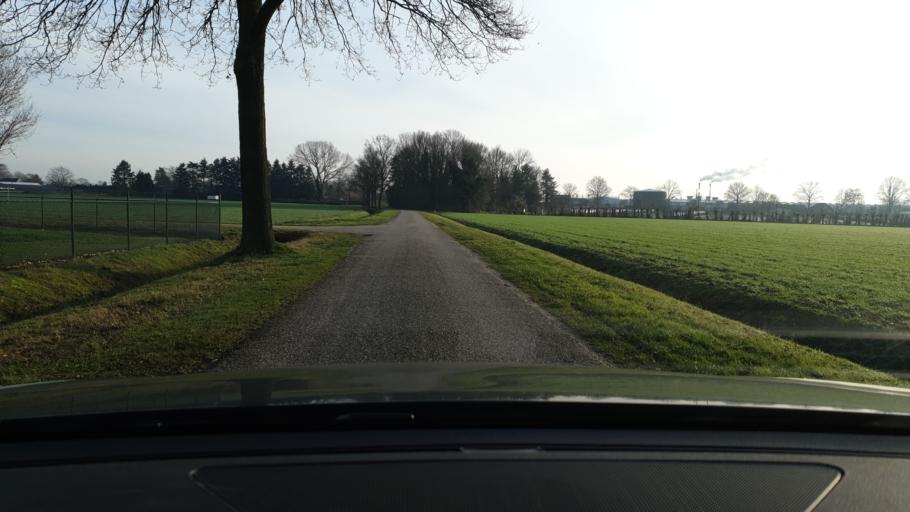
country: NL
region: Limburg
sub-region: Gemeente Venray
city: Venray
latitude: 51.4696
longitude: 6.0330
